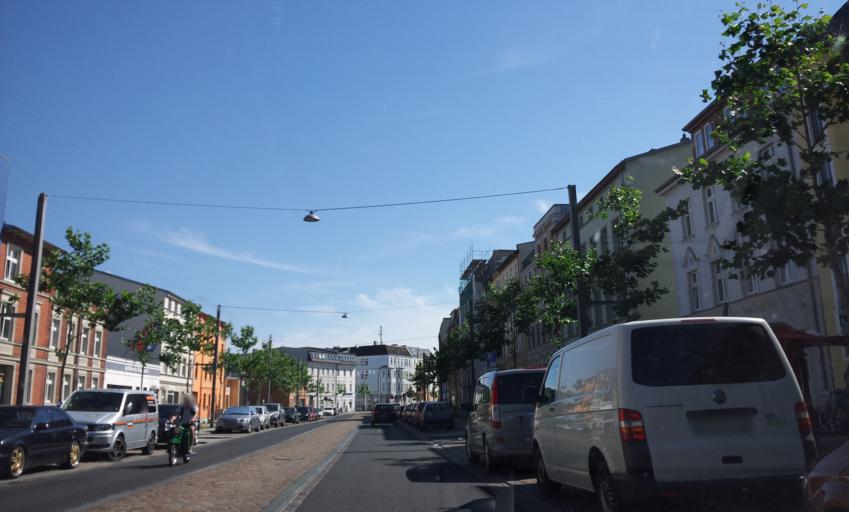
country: DE
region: Mecklenburg-Vorpommern
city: Stralsund
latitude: 54.3080
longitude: 13.0979
